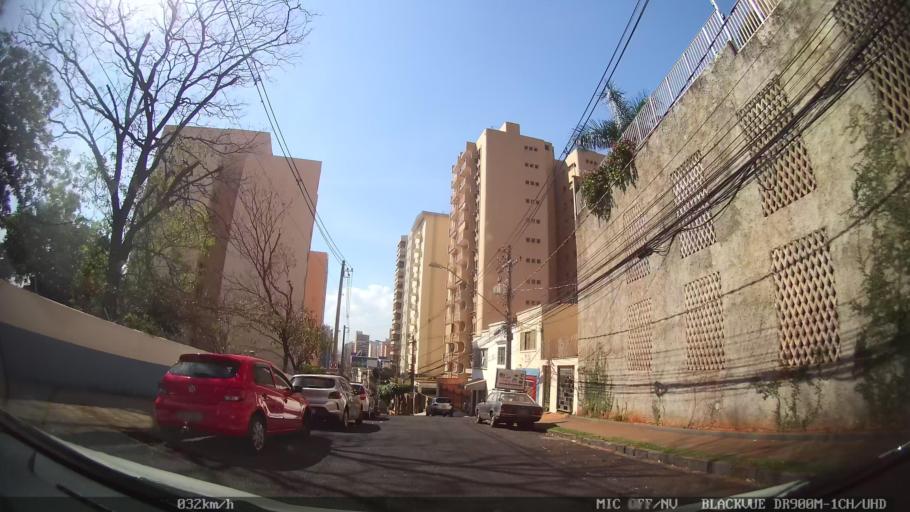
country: BR
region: Sao Paulo
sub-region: Ribeirao Preto
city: Ribeirao Preto
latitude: -21.1799
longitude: -47.8156
